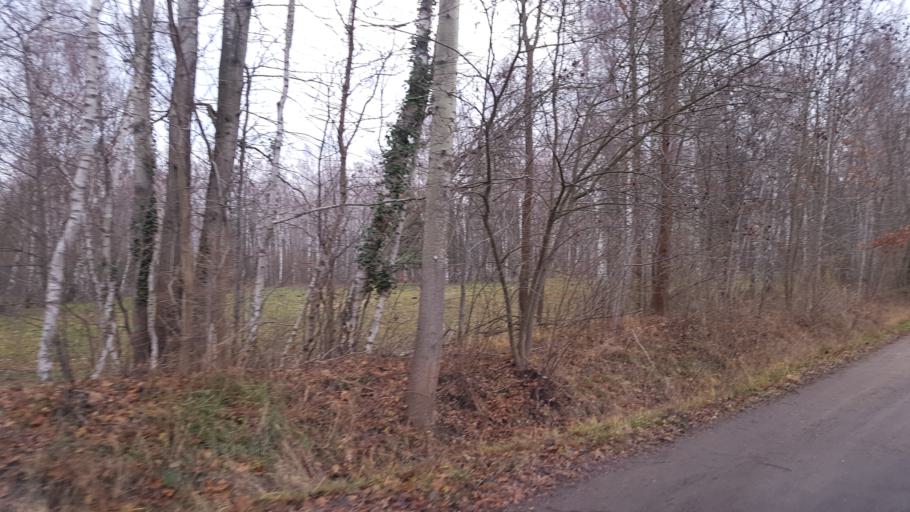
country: DE
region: Brandenburg
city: Sallgast
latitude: 51.5654
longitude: 13.8685
